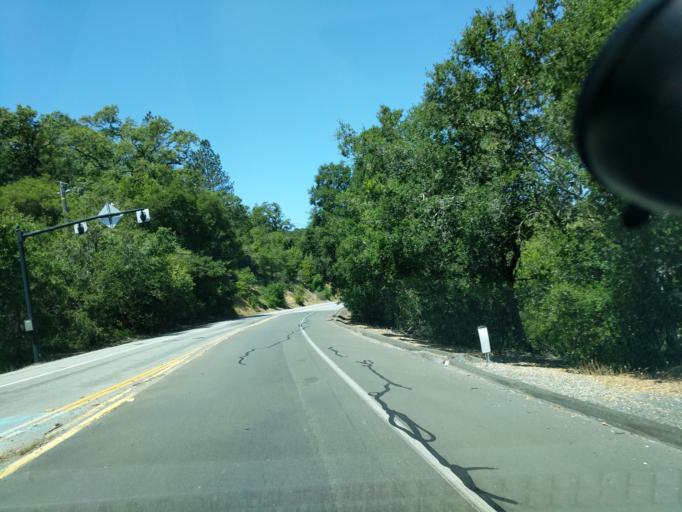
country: US
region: California
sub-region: Contra Costa County
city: Orinda
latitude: 37.9001
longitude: -122.2122
